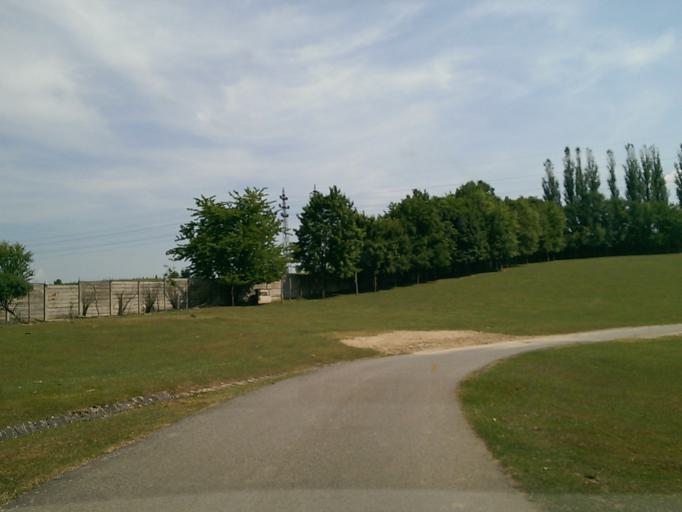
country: CZ
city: Bila Tremesna
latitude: 50.4349
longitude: 15.7745
